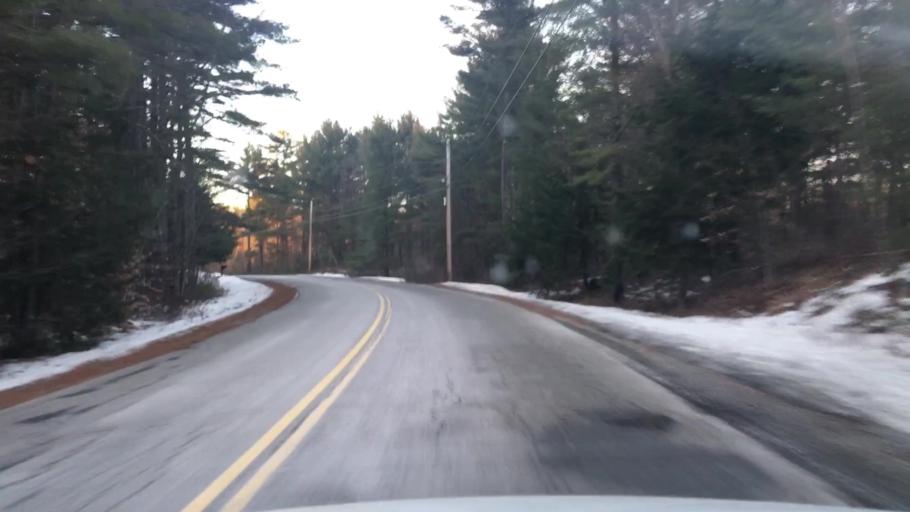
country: US
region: Maine
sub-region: York County
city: Lebanon
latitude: 43.3425
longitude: -70.8646
